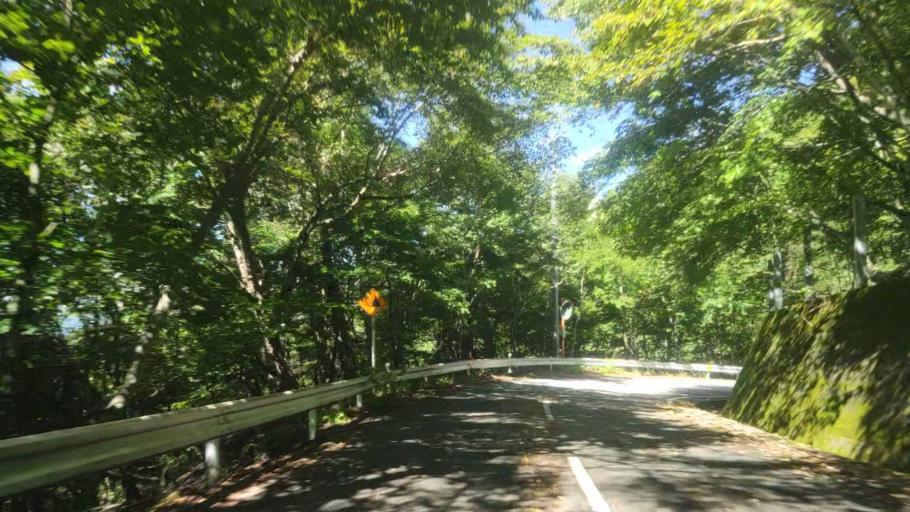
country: JP
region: Yamanashi
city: Fujikawaguchiko
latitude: 35.5622
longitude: 138.7858
